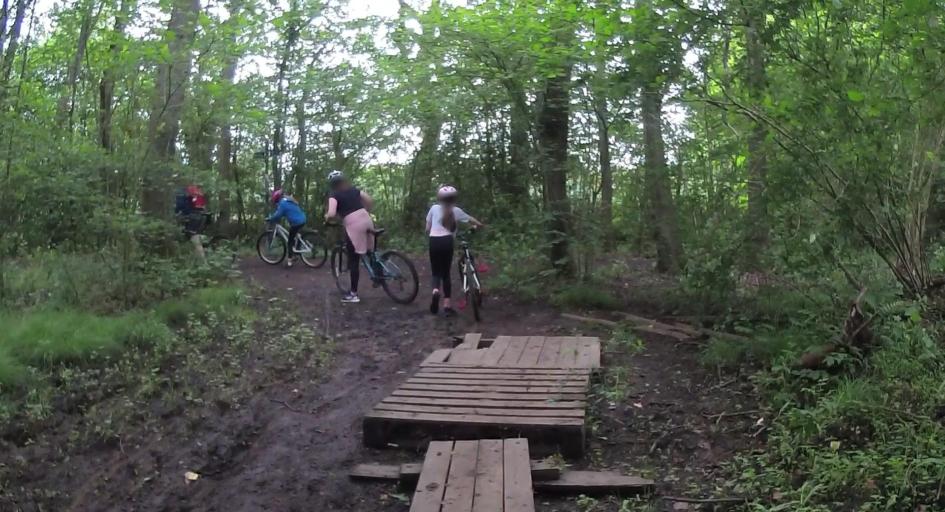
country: GB
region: England
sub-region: Wokingham
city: Finchampstead
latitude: 51.3576
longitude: -0.8667
